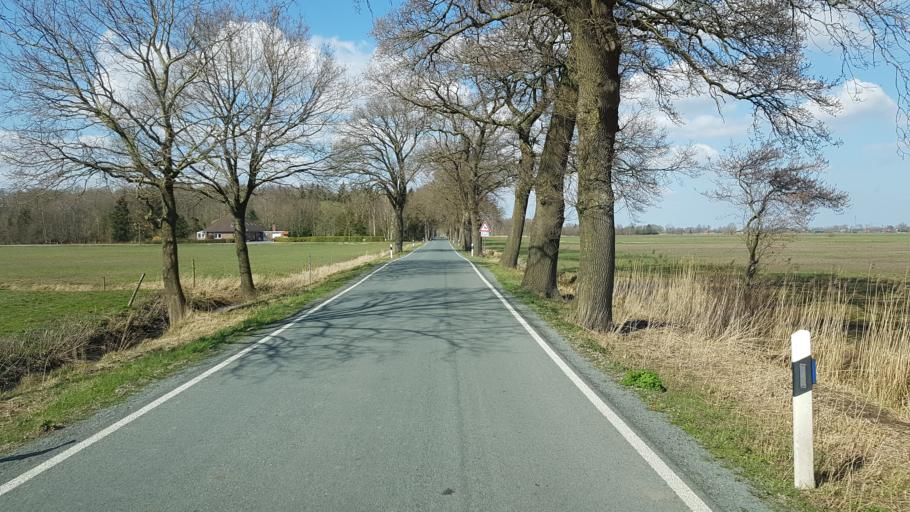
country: DE
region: Lower Saxony
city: Rastede
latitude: 53.3265
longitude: 8.2292
